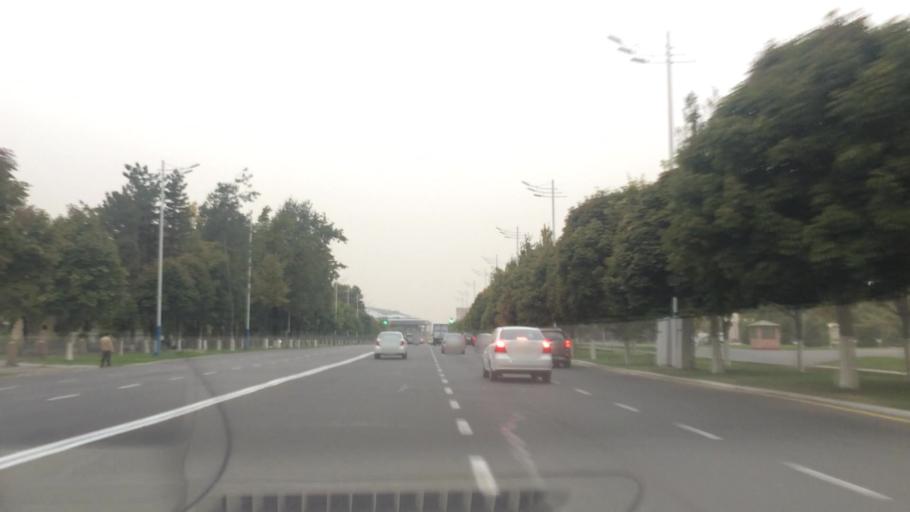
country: UZ
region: Toshkent Shahri
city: Tashkent
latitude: 41.3063
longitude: 69.2614
